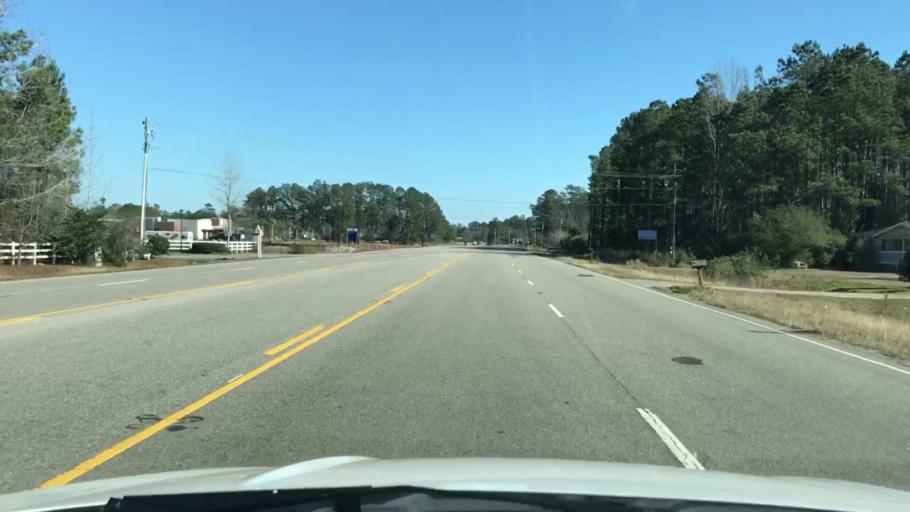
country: US
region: South Carolina
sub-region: Horry County
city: Garden City
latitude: 33.6298
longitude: -79.0295
